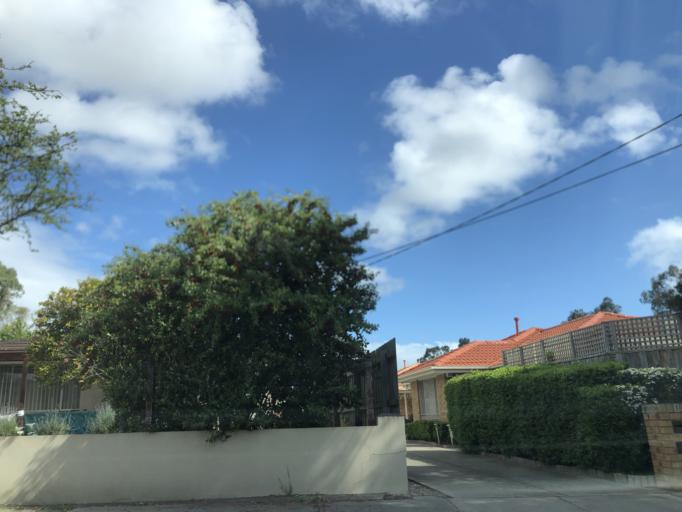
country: AU
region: Victoria
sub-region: Kingston
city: Clayton South
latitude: -37.9338
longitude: 145.1121
